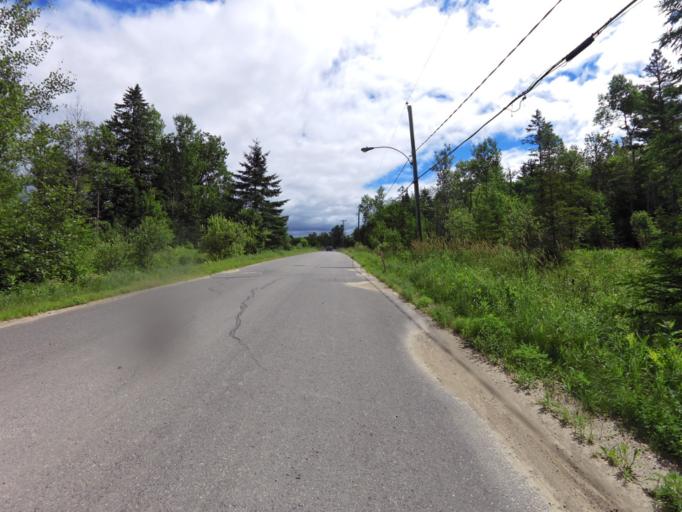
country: CA
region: Quebec
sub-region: Laurentides
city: Mont-Tremblant
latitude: 45.9655
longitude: -74.6198
